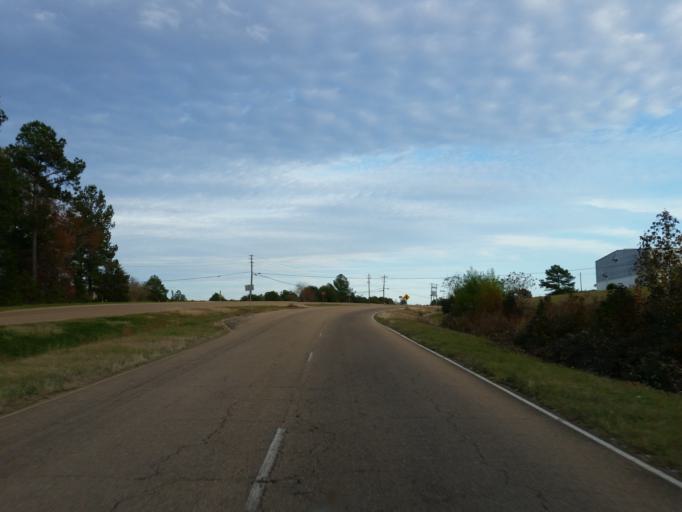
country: US
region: Mississippi
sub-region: Lauderdale County
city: Marion
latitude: 32.4127
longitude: -88.6345
